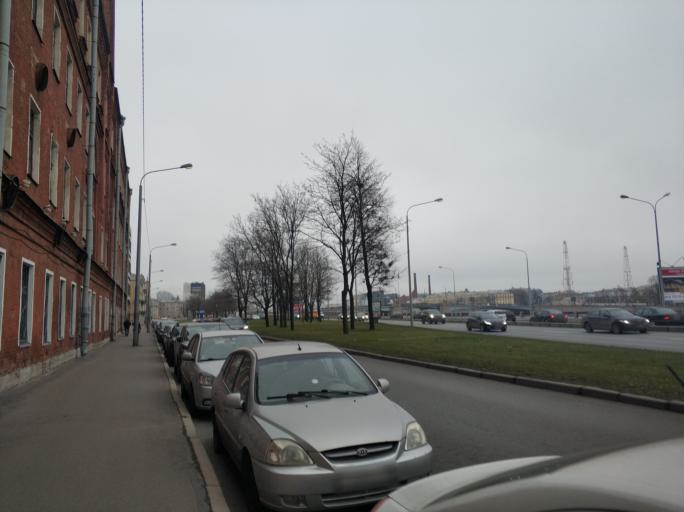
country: RU
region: Leningrad
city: Sampsonievskiy
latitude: 59.9715
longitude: 30.3358
